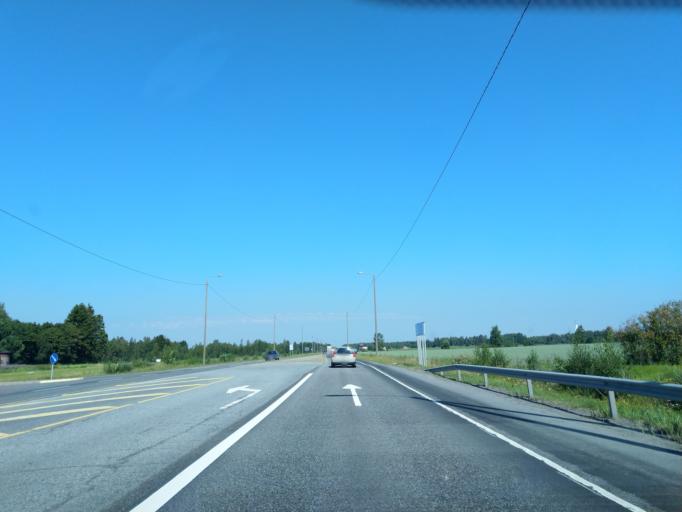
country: FI
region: Satakunta
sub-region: Pori
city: Nakkila
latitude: 61.3511
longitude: 22.0128
